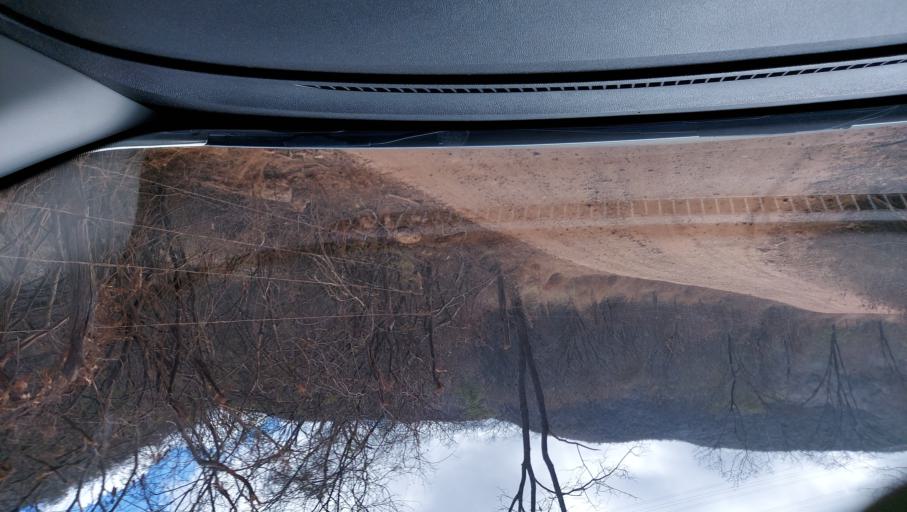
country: BR
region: Bahia
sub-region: Oliveira Dos Brejinhos
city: Beira Rio
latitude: -12.0966
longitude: -42.5448
